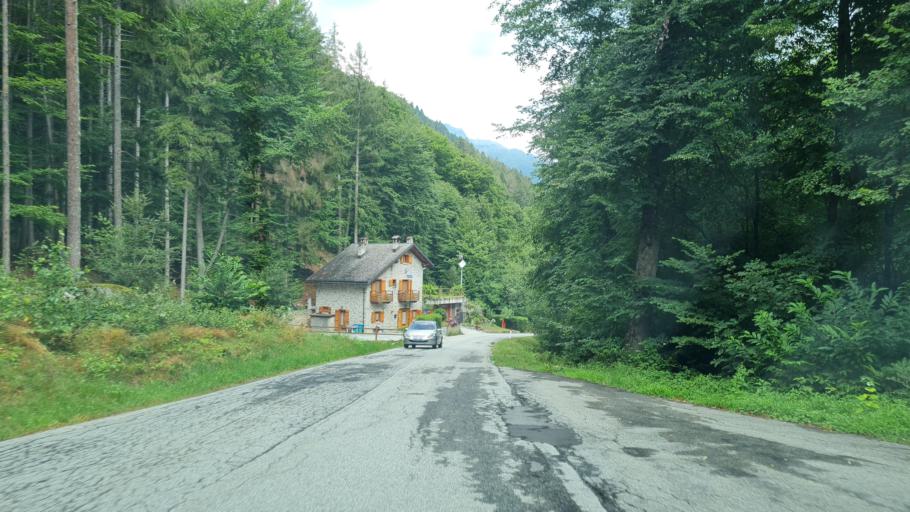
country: IT
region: Piedmont
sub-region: Provincia Verbano-Cusio-Ossola
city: Baceno
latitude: 46.2467
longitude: 8.3158
